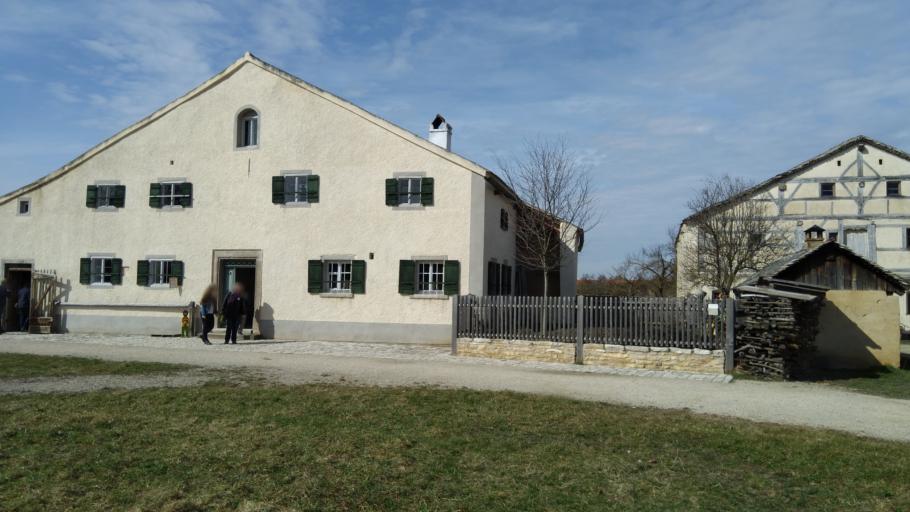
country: DE
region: Bavaria
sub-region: Regierungsbezirk Mittelfranken
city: Bad Windsheim
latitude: 49.4947
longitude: 10.4266
